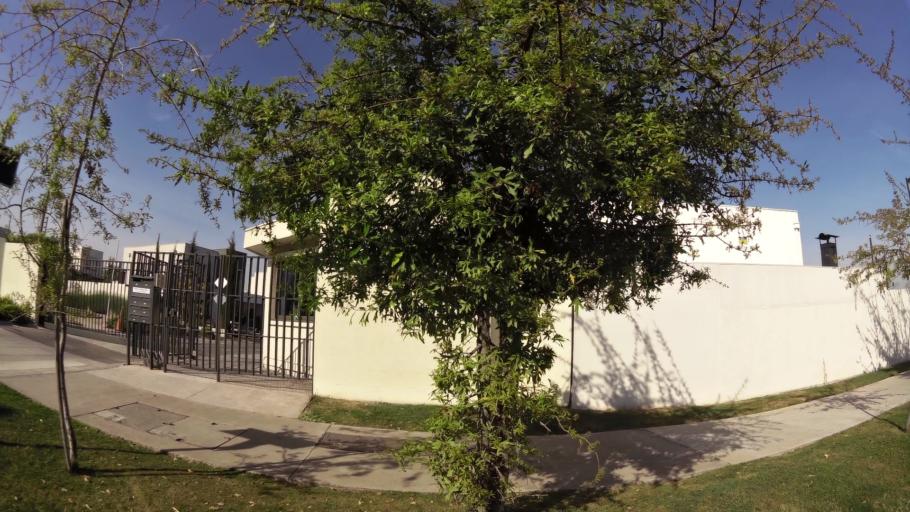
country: CL
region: Santiago Metropolitan
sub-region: Provincia de Santiago
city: Villa Presidente Frei, Nunoa, Santiago, Chile
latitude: -33.4929
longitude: -70.5557
